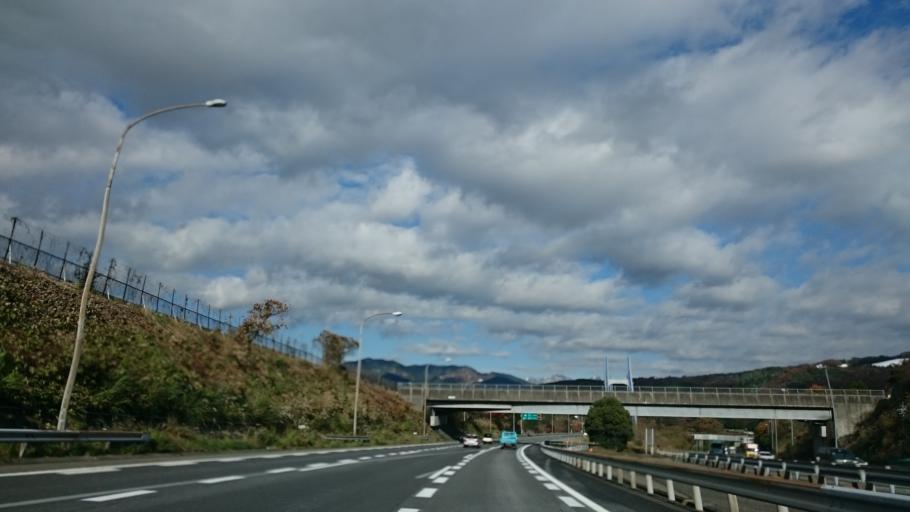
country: JP
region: Shizuoka
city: Gotemba
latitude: 35.3372
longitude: 138.9735
